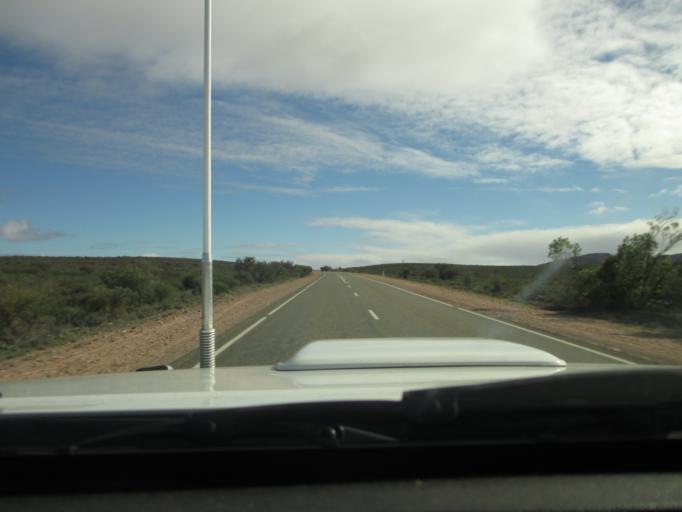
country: AU
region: South Australia
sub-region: Flinders Ranges
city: Quorn
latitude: -31.8156
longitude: 138.3727
